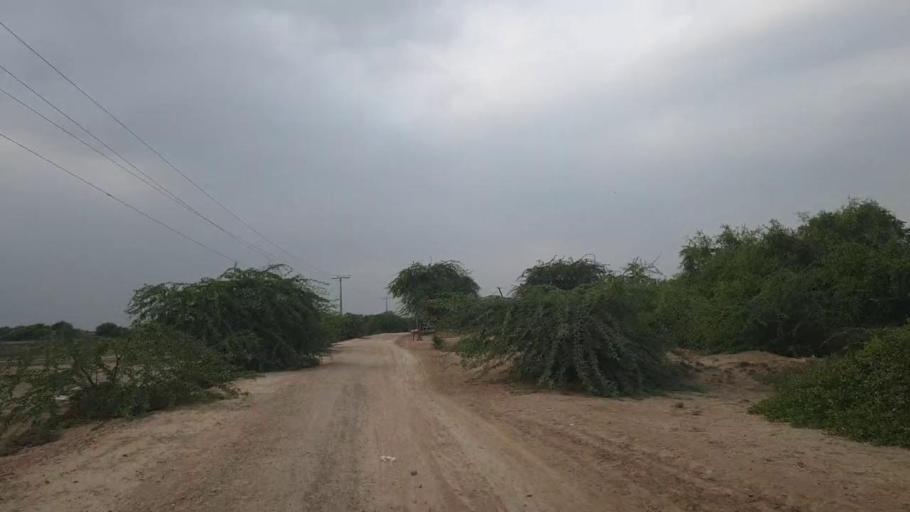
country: PK
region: Sindh
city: Badin
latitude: 24.6150
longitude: 68.6833
